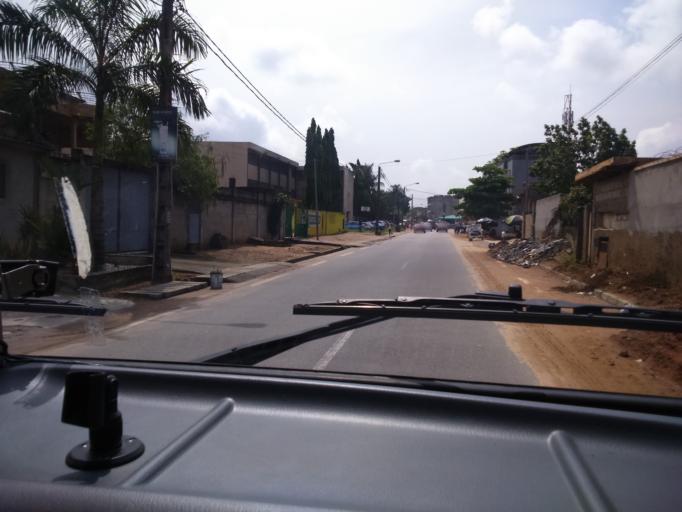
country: CI
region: Lagunes
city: Abidjan
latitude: 5.3557
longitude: -3.9791
